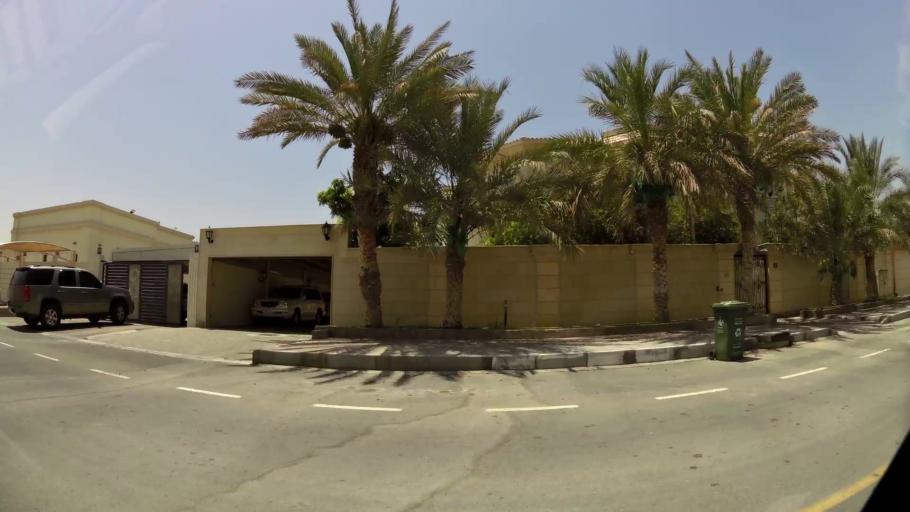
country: AE
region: Dubai
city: Dubai
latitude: 25.0874
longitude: 55.2088
